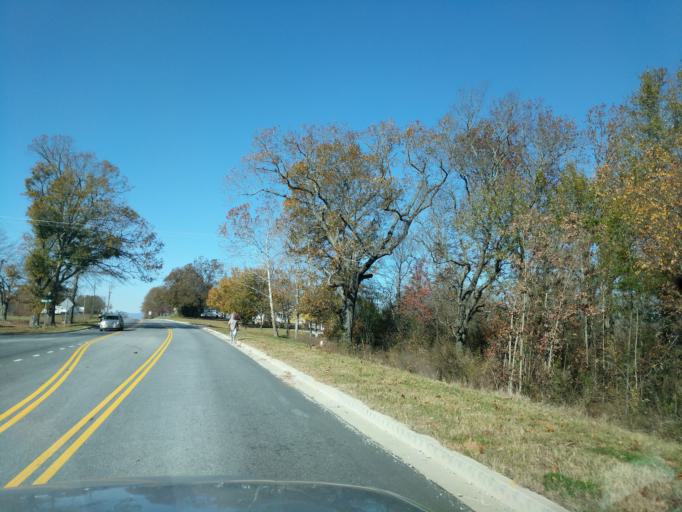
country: US
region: South Carolina
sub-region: Greenville County
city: Tigerville
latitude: 34.9948
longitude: -82.3464
